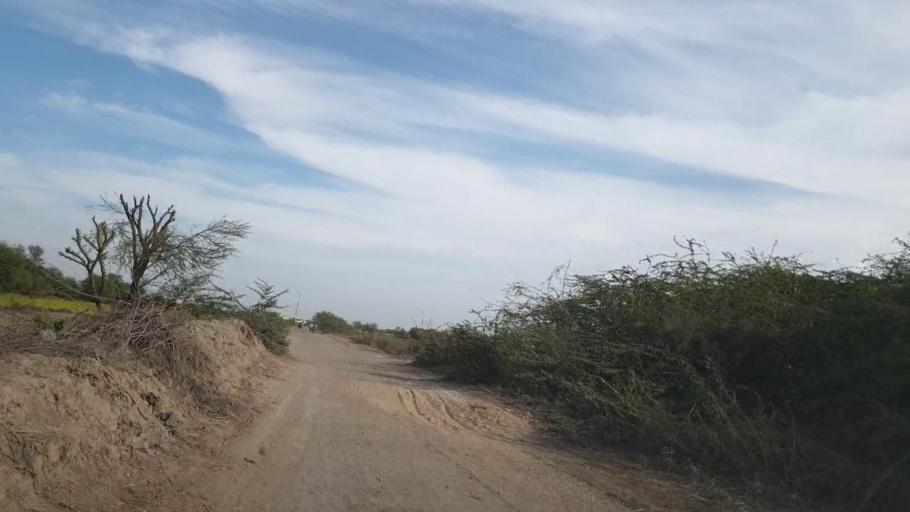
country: PK
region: Sindh
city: Pithoro
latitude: 25.6302
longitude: 69.4081
